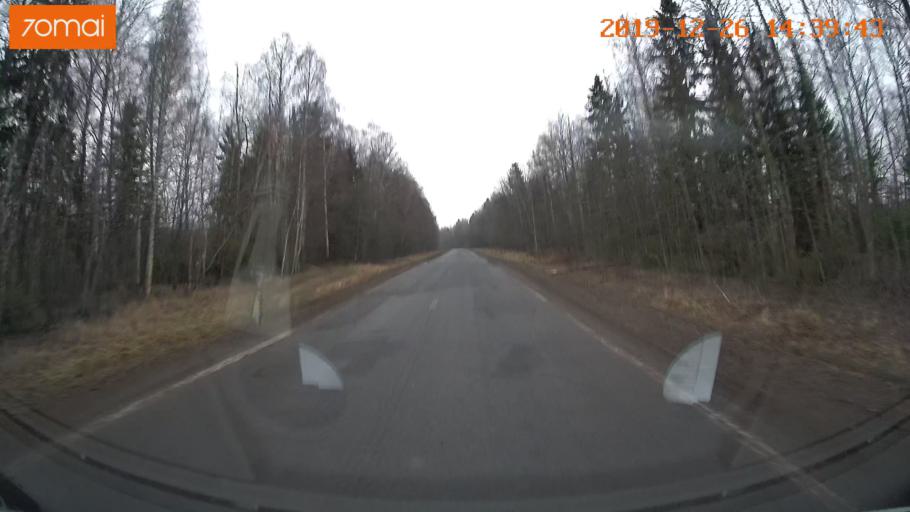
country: RU
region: Jaroslavl
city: Poshekhon'ye
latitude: 58.3805
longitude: 38.9842
